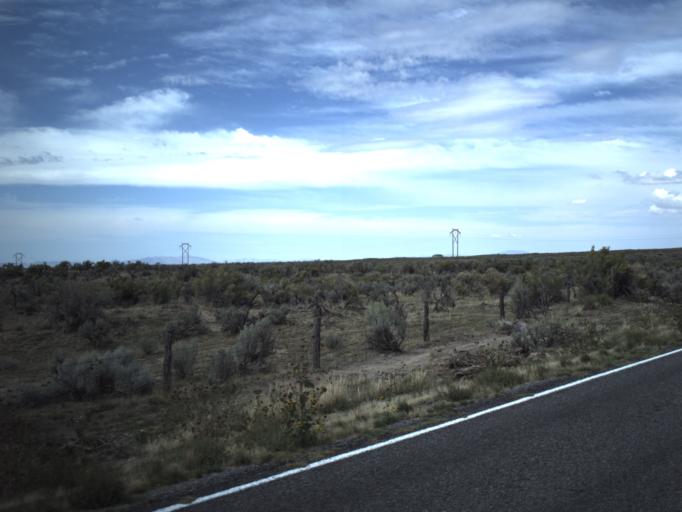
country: US
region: Utah
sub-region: Millard County
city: Fillmore
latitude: 39.1499
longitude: -112.4098
